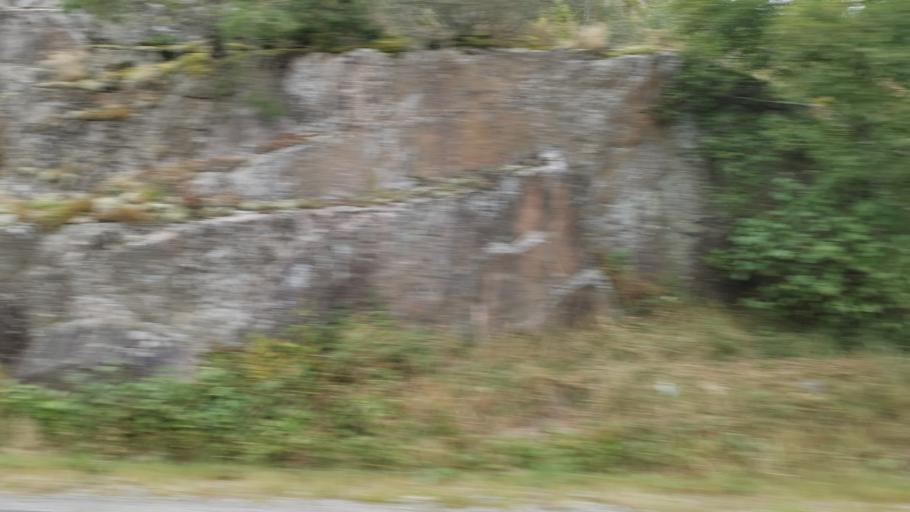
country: SE
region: Vaestra Goetaland
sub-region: Tanums Kommun
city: Tanumshede
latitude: 58.6583
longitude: 11.3459
